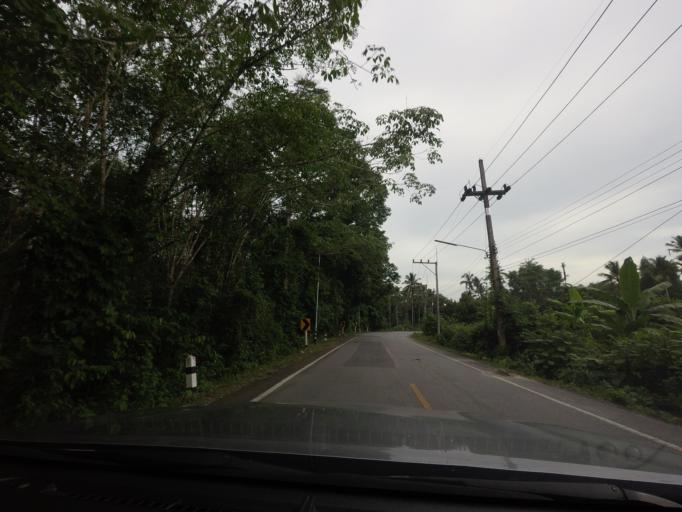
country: TH
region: Yala
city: Raman
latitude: 6.4355
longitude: 101.4546
